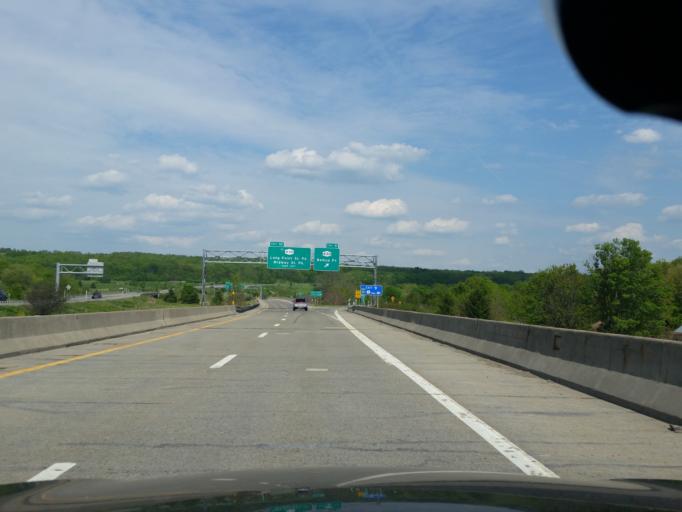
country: US
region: New York
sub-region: Chautauqua County
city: Lakewood
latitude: 42.1520
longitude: -79.3849
